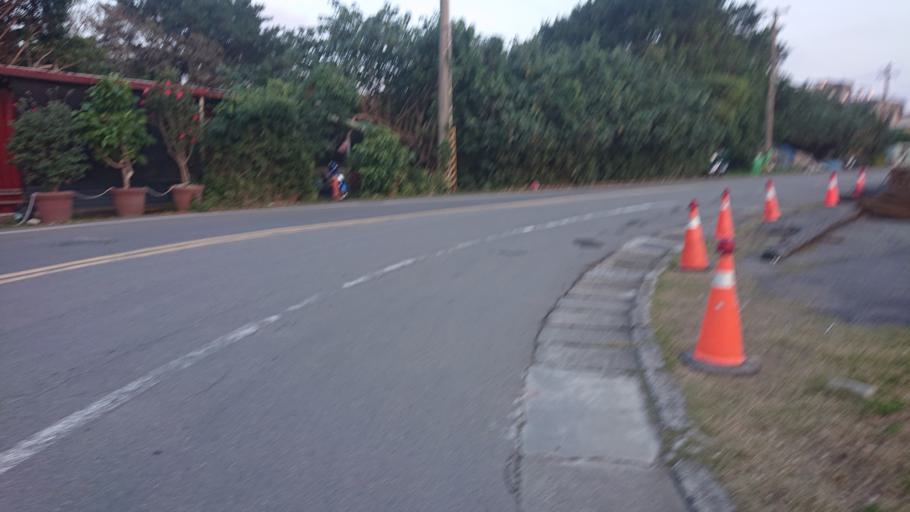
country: TW
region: Taipei
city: Taipei
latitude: 25.1889
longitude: 121.4193
